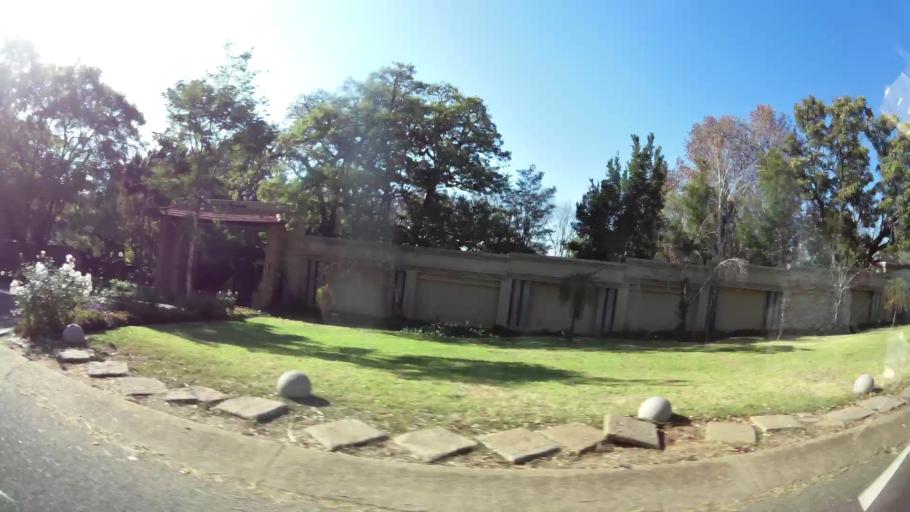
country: ZA
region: Gauteng
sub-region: City of Johannesburg Metropolitan Municipality
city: Midrand
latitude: -26.0521
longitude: 28.0338
